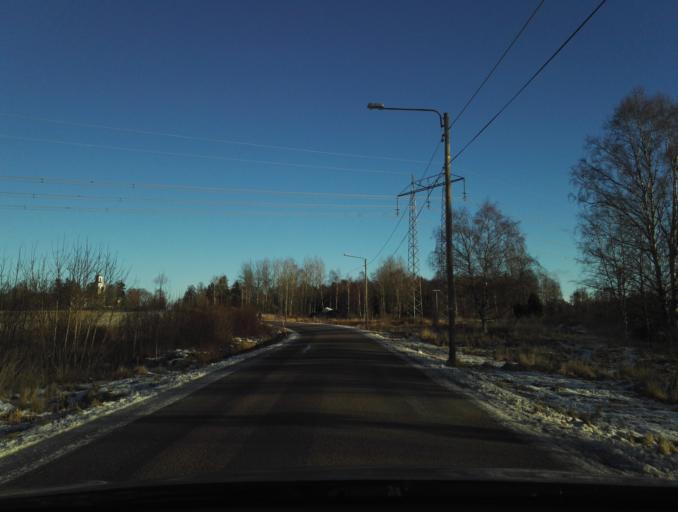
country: SE
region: Kronoberg
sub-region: Vaxjo Kommun
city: Gemla
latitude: 56.8466
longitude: 14.6106
